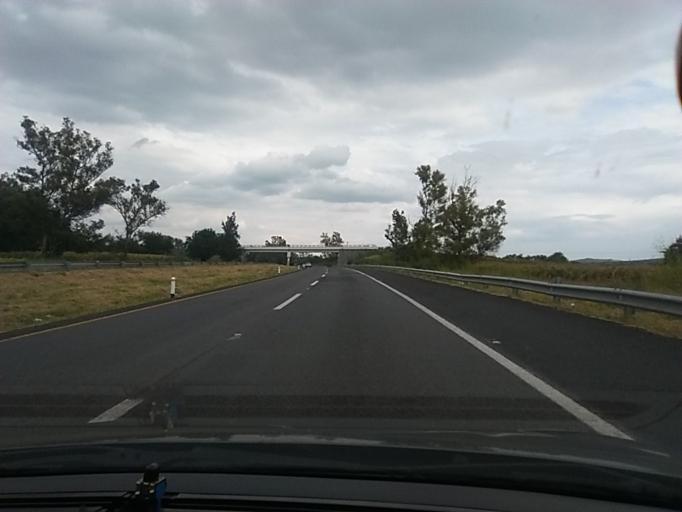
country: MX
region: Jalisco
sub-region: Ocotlan
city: Joconoxtle (La Tuna)
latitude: 20.3827
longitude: -102.7037
